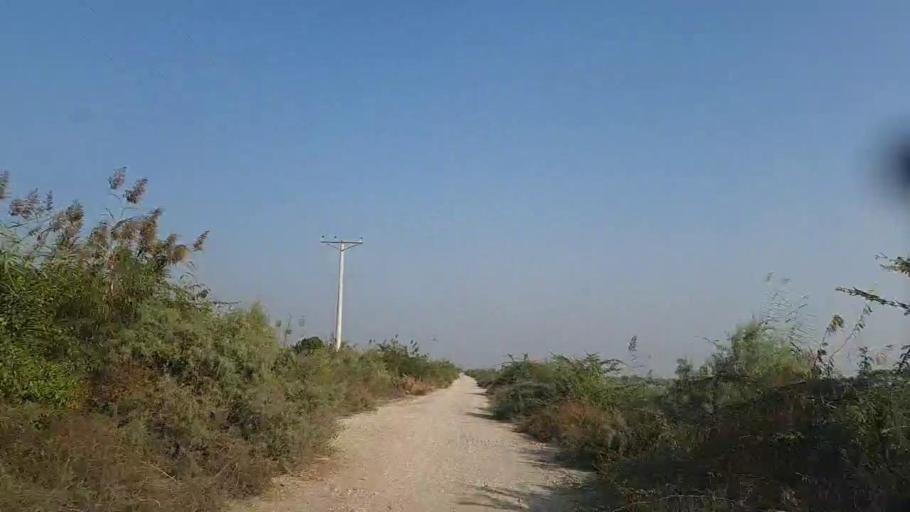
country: PK
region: Sindh
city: Jati
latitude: 24.4602
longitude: 68.3105
